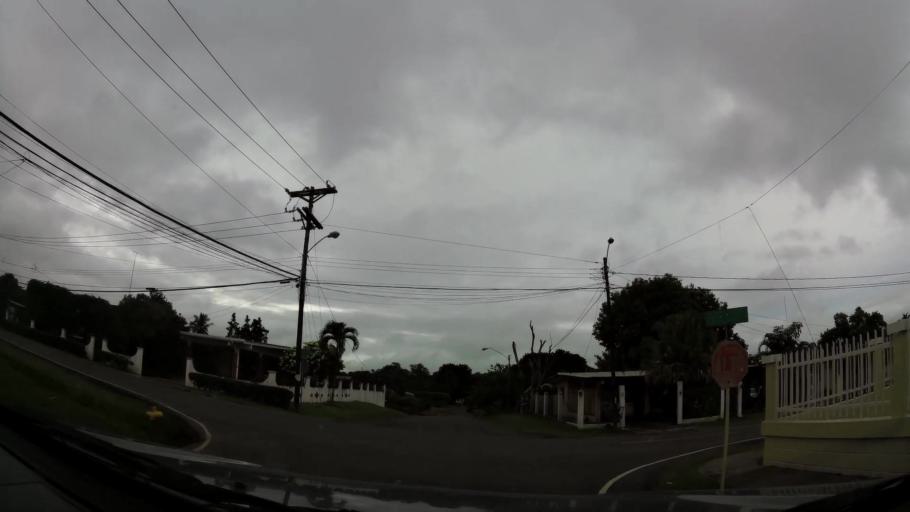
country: PA
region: Chiriqui
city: La Concepcion
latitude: 8.5160
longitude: -82.6179
